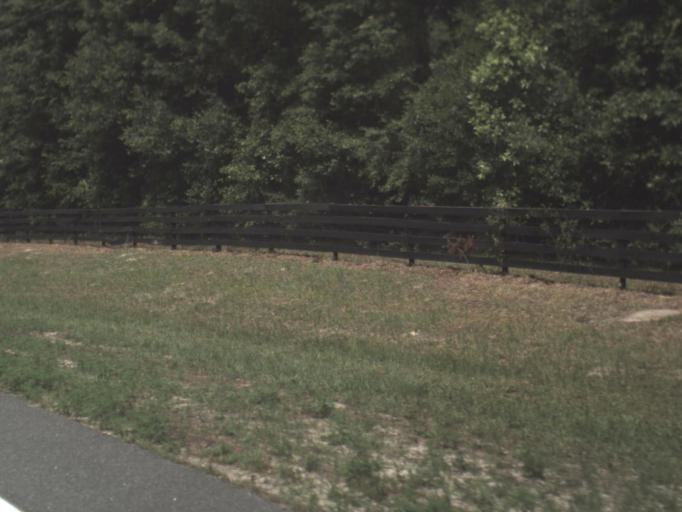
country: US
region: Florida
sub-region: Levy County
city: Williston
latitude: 29.4219
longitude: -82.4249
